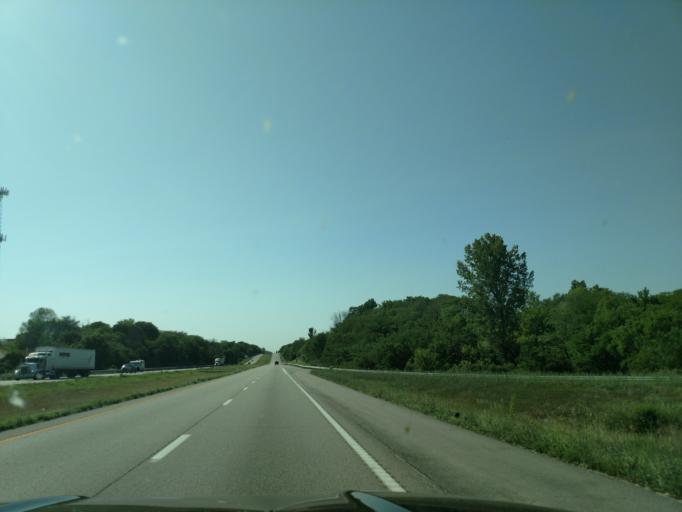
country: US
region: Missouri
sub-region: Andrew County
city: Savannah
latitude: 39.9192
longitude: -94.9087
